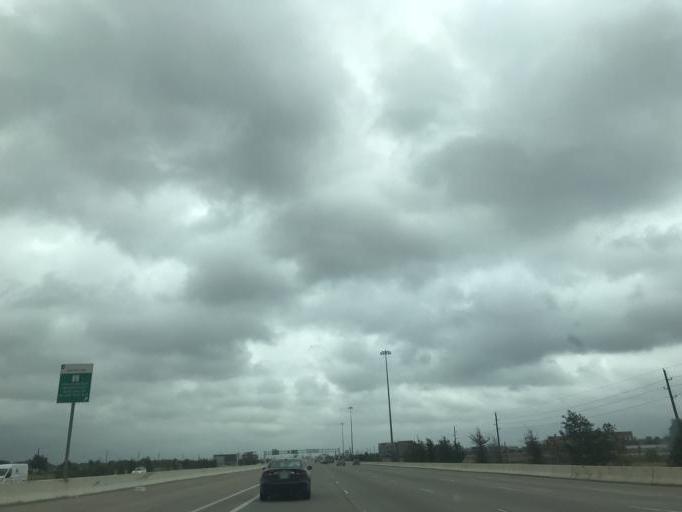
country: US
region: Texas
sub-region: Fort Bend County
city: Greatwood
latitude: 29.5739
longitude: -95.6594
